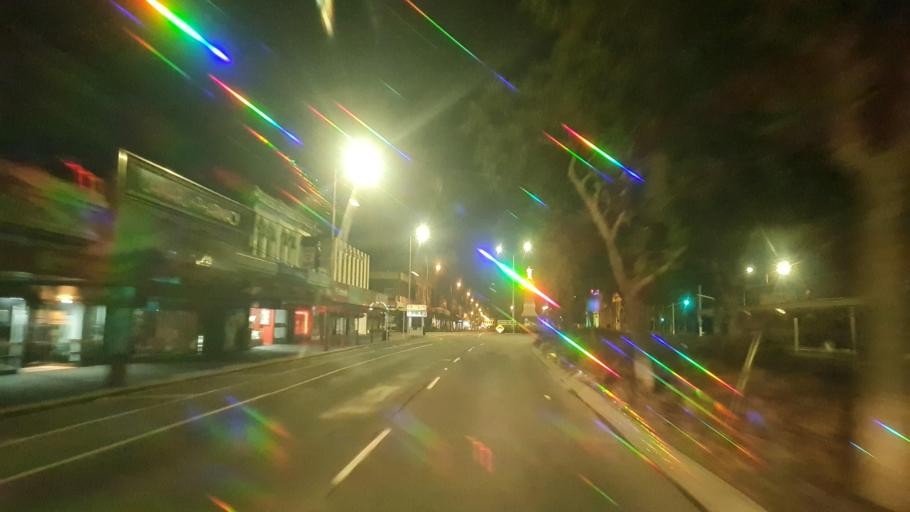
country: NZ
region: Otago
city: Oamaru
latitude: -45.0968
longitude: 170.9715
